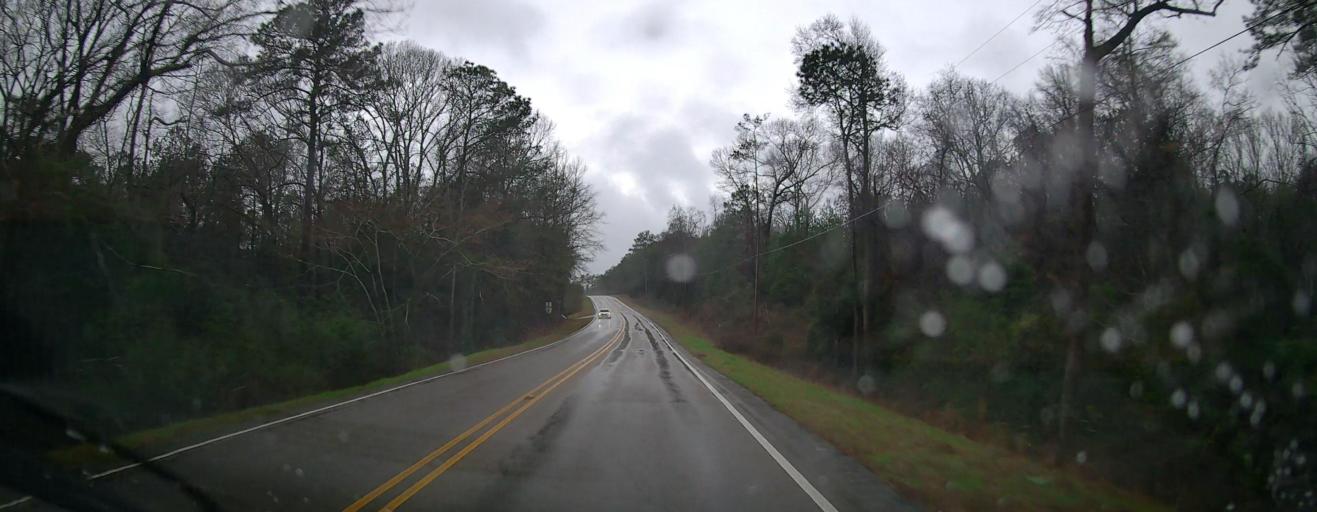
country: US
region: Alabama
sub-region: Autauga County
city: Pine Level
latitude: 32.5190
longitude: -86.6029
